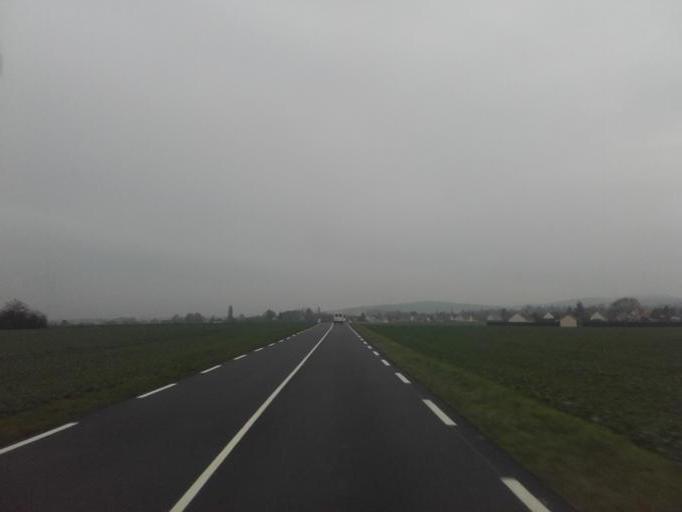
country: FR
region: Bourgogne
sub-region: Departement de Saone-et-Loire
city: Rully
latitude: 46.8875
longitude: 4.7523
